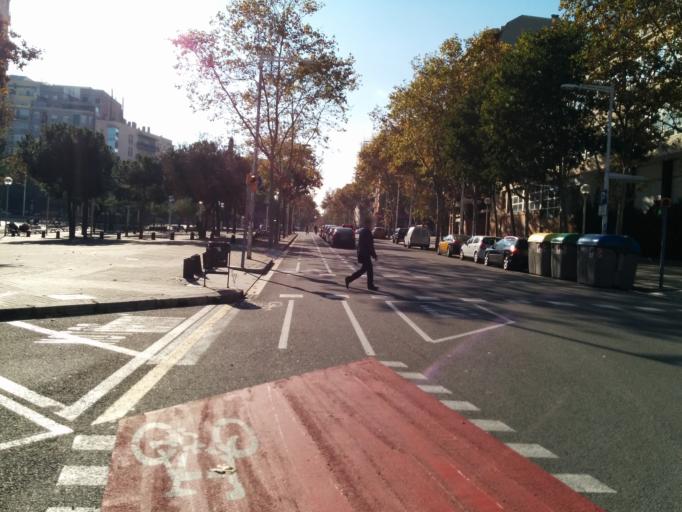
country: ES
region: Catalonia
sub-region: Provincia de Barcelona
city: Ciutat Vella
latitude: 41.3939
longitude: 2.1903
